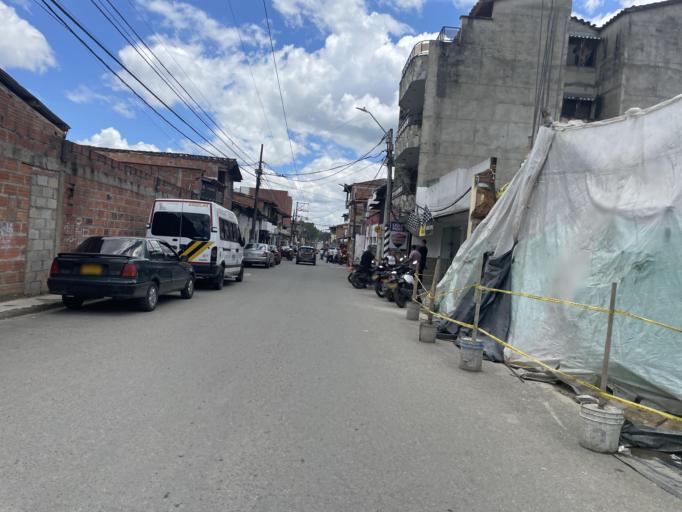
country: CO
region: Antioquia
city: La Ceja
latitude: 6.0342
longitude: -75.4302
